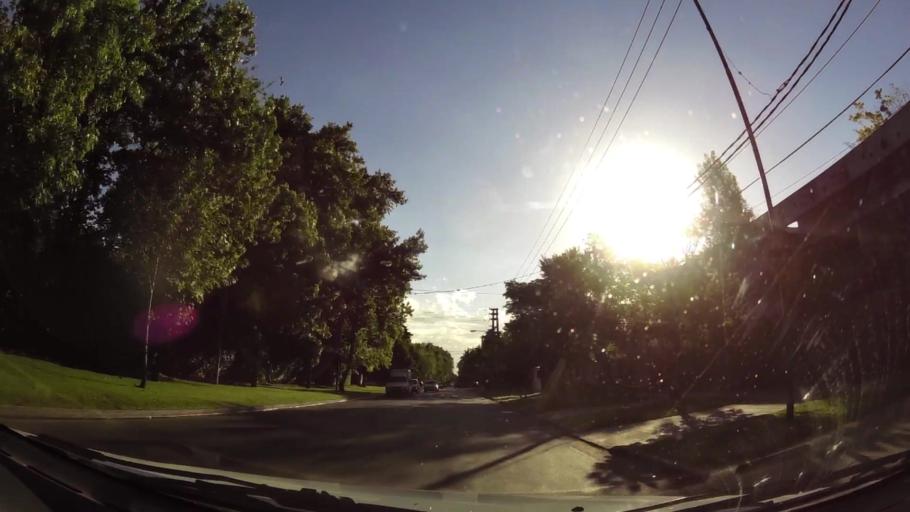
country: AR
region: Buenos Aires
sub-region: Partido de San Isidro
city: San Isidro
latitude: -34.4818
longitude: -58.5380
